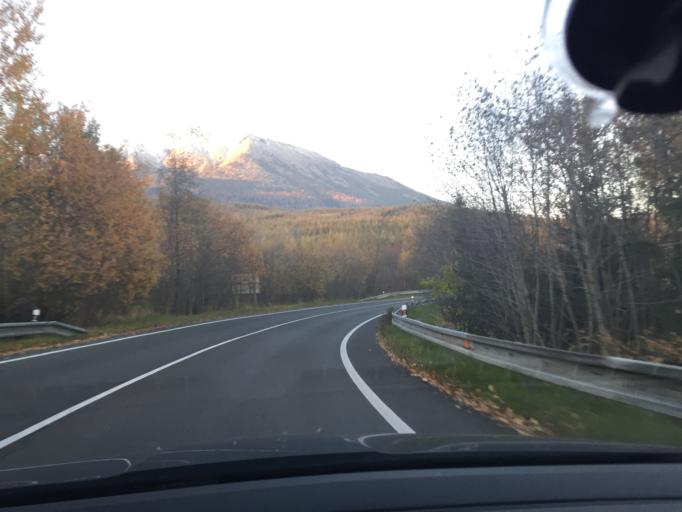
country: SK
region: Presovsky
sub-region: Okres Poprad
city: Vysoke Tatry
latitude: 49.1248
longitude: 20.1864
